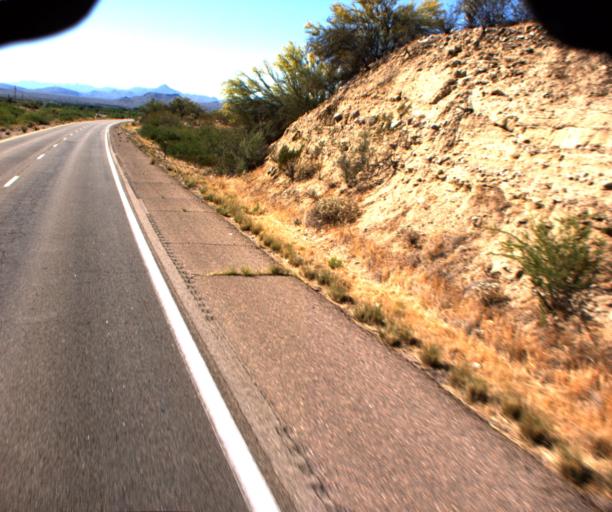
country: US
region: Arizona
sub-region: Yavapai County
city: Bagdad
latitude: 34.6749
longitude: -113.5905
